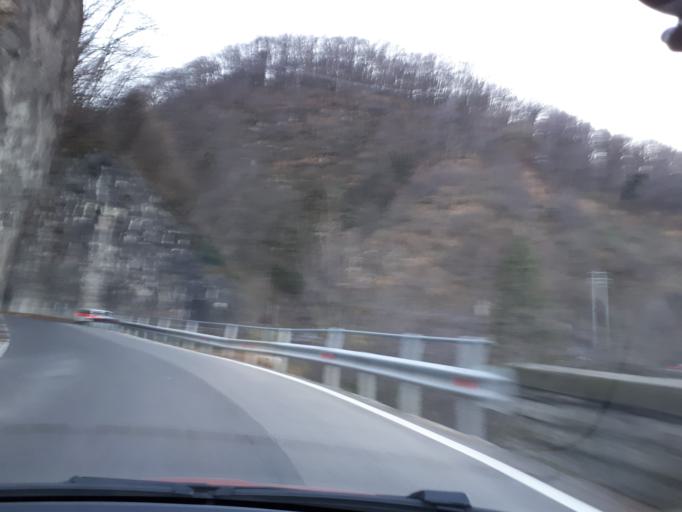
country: IT
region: Lombardy
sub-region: Provincia di Como
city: Faggeto Lario
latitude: 45.8574
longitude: 9.1409
